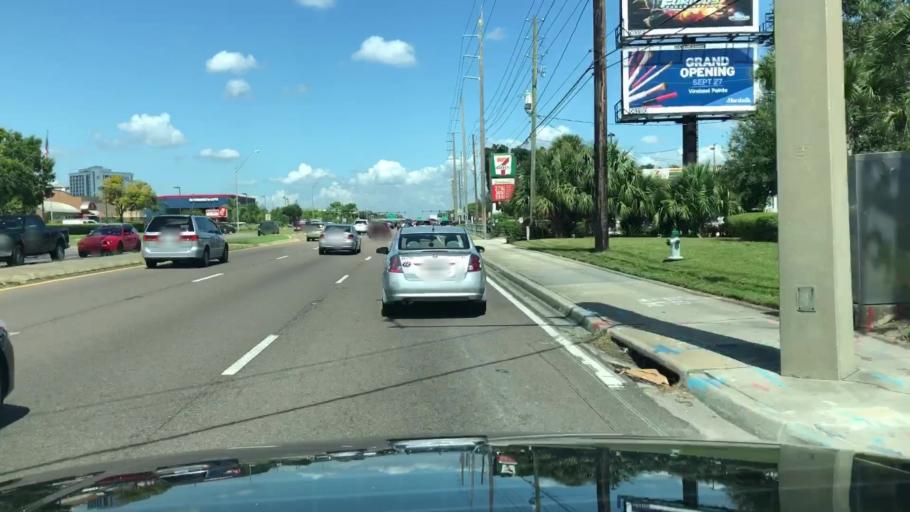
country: US
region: Florida
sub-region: Osceola County
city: Celebration
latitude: 28.3708
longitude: -81.5032
